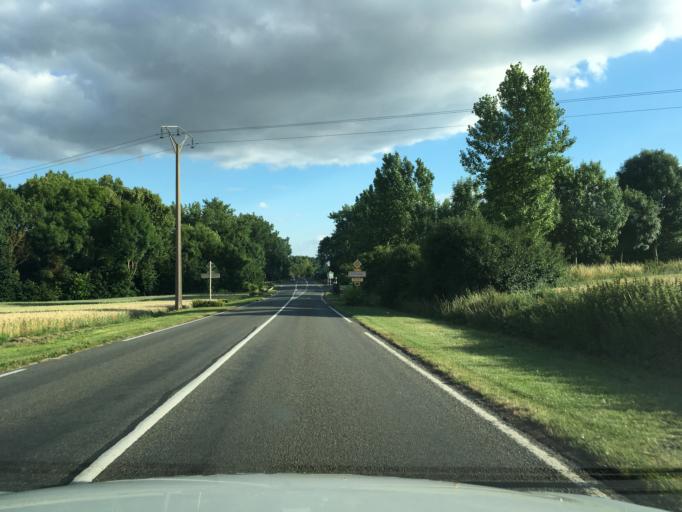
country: FR
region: Picardie
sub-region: Departement de la Somme
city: Peronne
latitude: 49.9389
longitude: 2.9490
